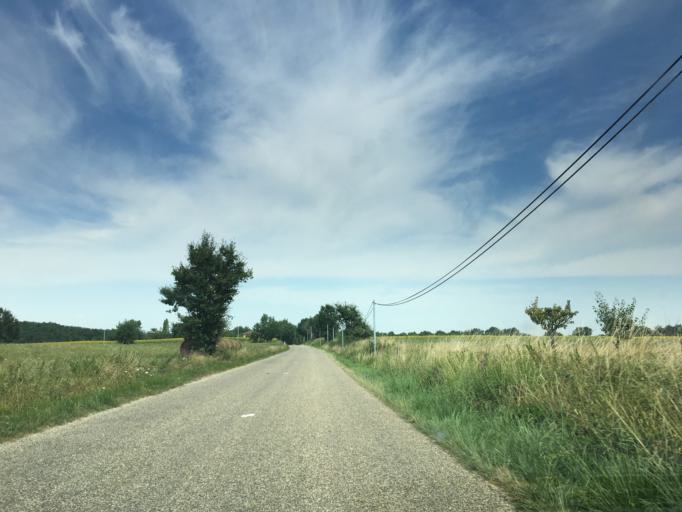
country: FR
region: Midi-Pyrenees
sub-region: Departement du Gers
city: Fleurance
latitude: 43.8181
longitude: 0.6337
